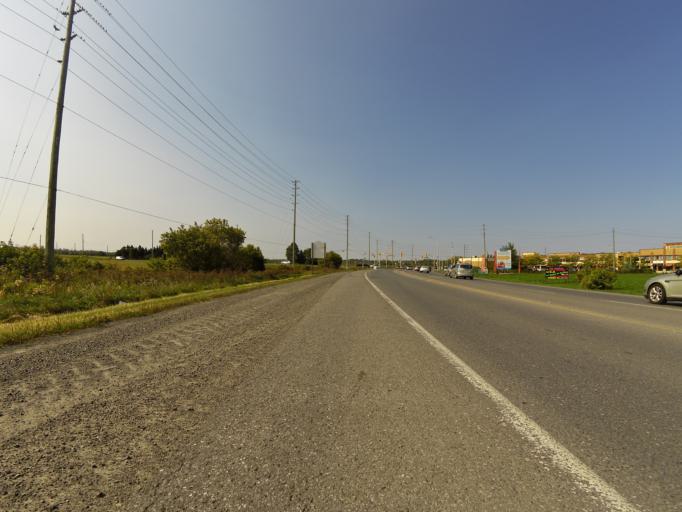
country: CA
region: Ontario
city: Bells Corners
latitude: 45.2597
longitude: -75.7658
